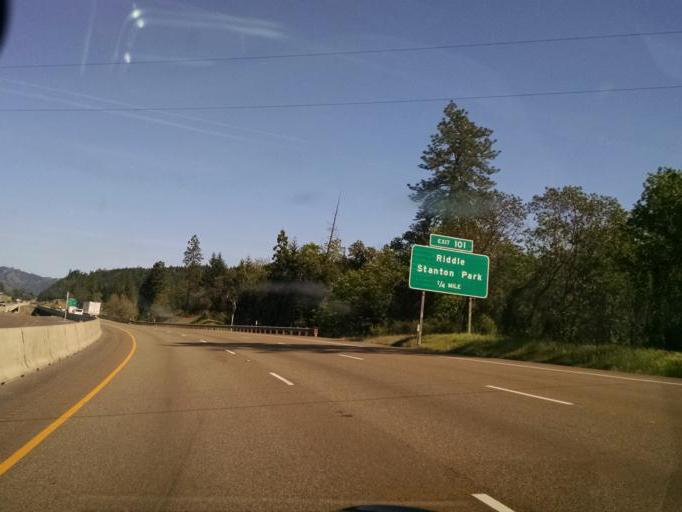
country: US
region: Oregon
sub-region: Douglas County
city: Riddle
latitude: 42.9479
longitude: -123.3272
